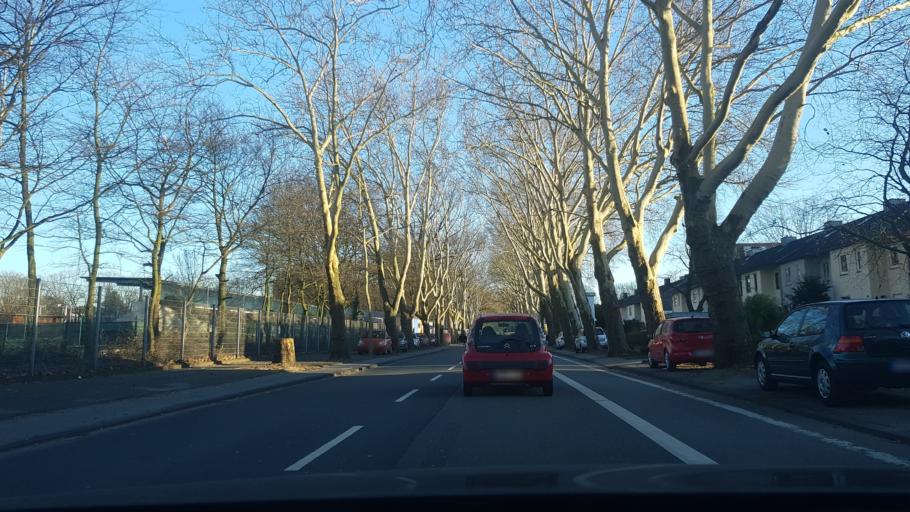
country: DE
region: North Rhine-Westphalia
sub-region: Regierungsbezirk Dusseldorf
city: Hochfeld
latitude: 51.4057
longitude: 6.7775
